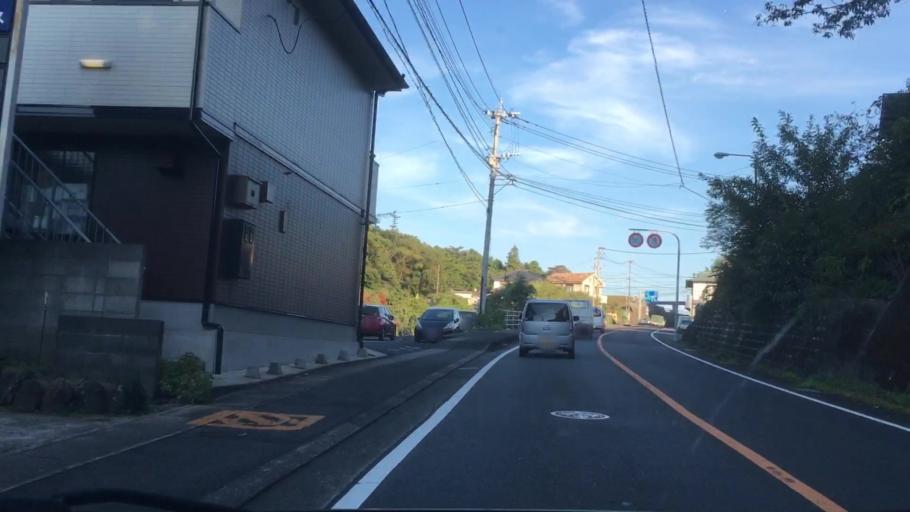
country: JP
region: Nagasaki
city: Sasebo
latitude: 33.0441
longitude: 129.7393
